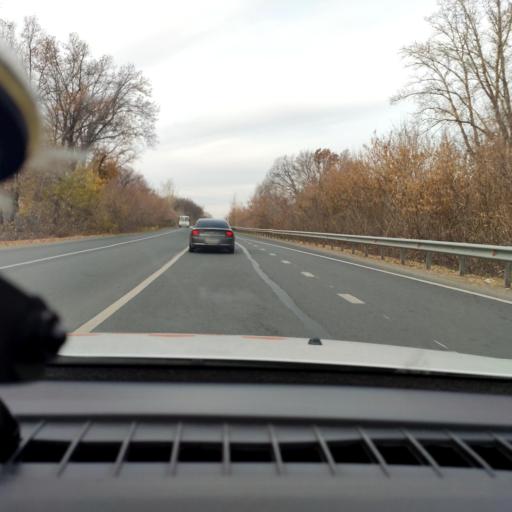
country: RU
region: Samara
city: Novokuybyshevsk
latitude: 53.1451
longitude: 50.0067
